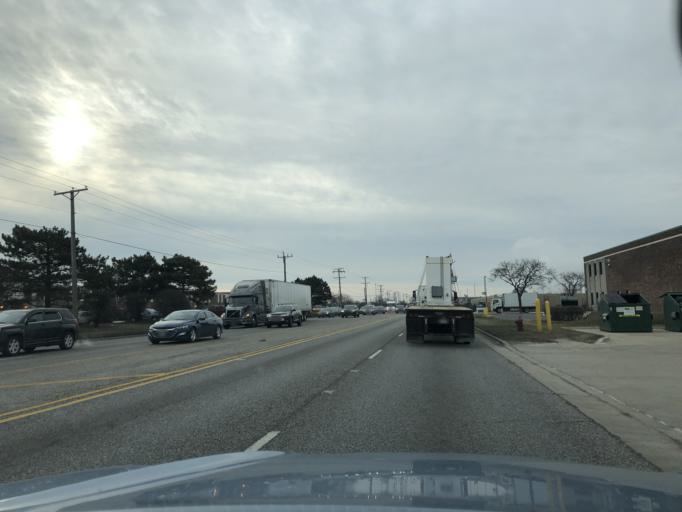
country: US
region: Illinois
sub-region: Cook County
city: Elk Grove Village
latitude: 42.0035
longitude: -87.9402
